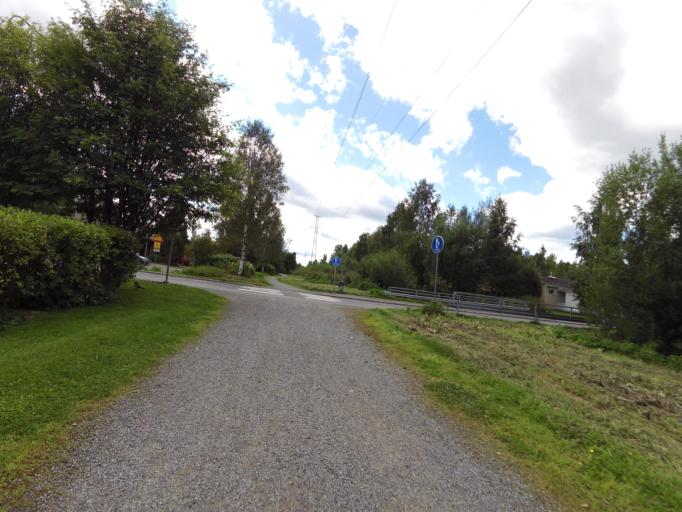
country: FI
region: Pirkanmaa
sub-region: Tampere
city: Yloejaervi
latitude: 61.5127
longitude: 23.6078
